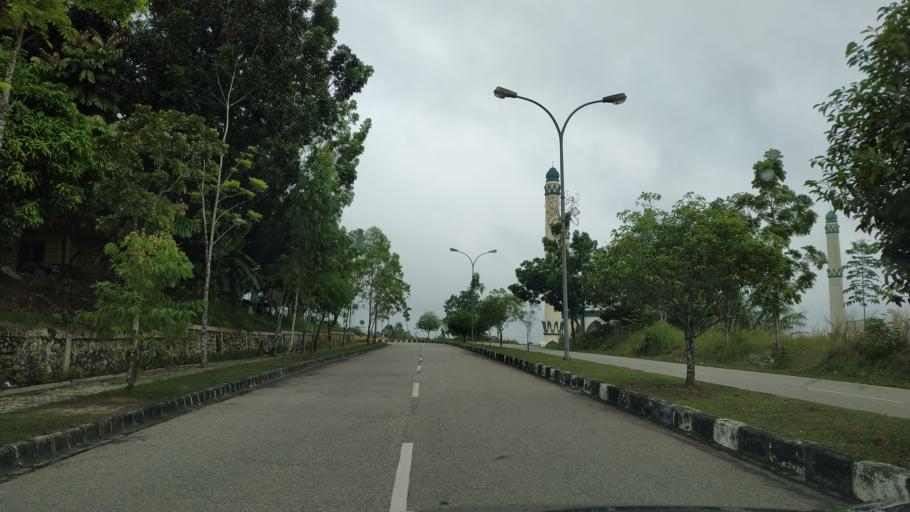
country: ID
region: Riau
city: Pangkalanbunut
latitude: 0.3818
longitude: 101.8293
